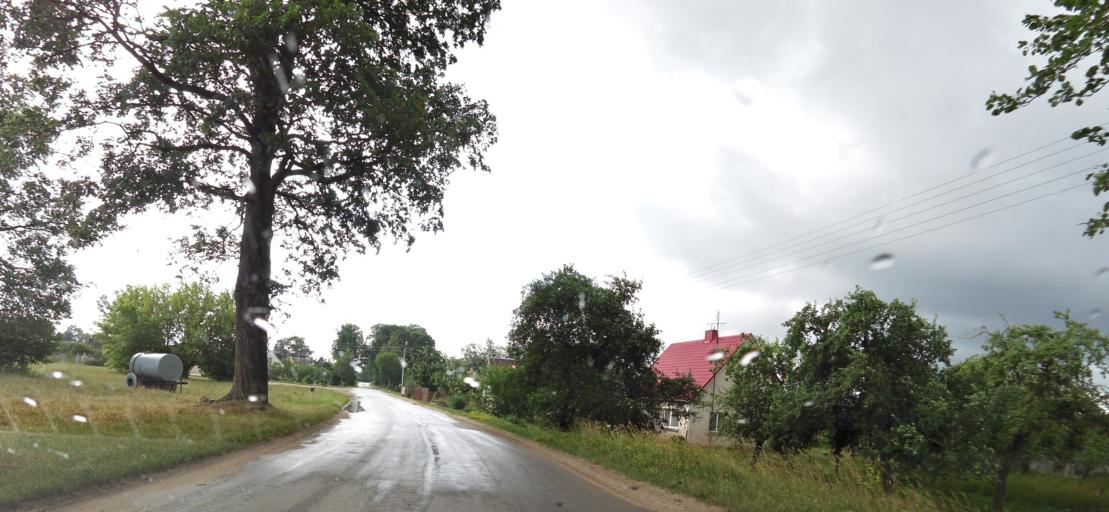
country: LT
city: Vabalninkas
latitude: 55.8848
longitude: 24.7844
